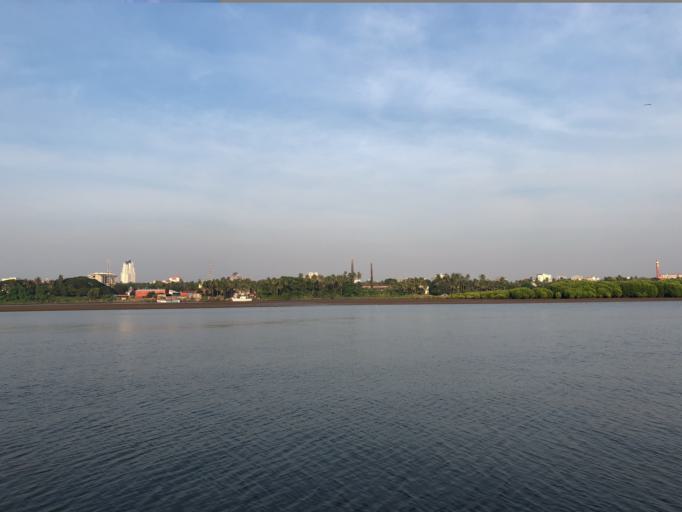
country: IN
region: Karnataka
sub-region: Dakshina Kannada
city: Mangalore
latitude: 12.8785
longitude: 74.8212
